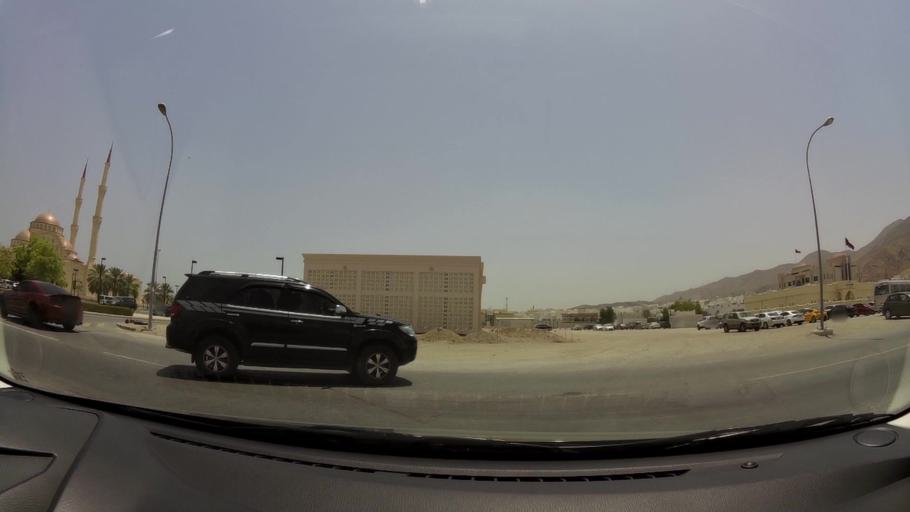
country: OM
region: Muhafazat Masqat
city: Bawshar
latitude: 23.5823
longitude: 58.4304
